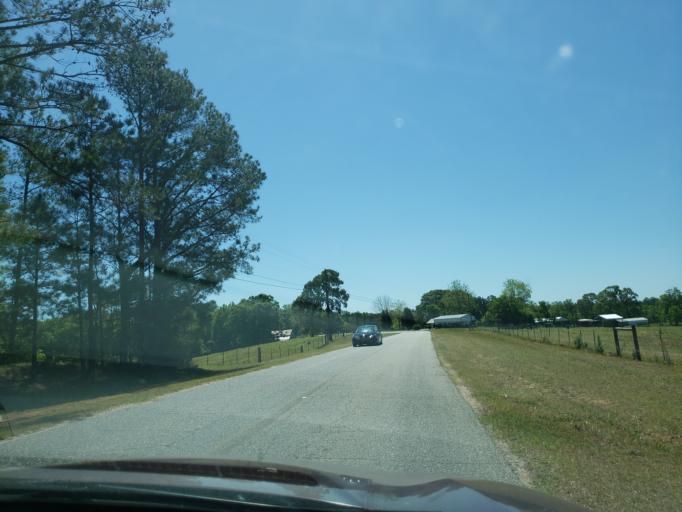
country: US
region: Alabama
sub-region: Tallapoosa County
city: Dadeville
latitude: 32.6988
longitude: -85.8589
